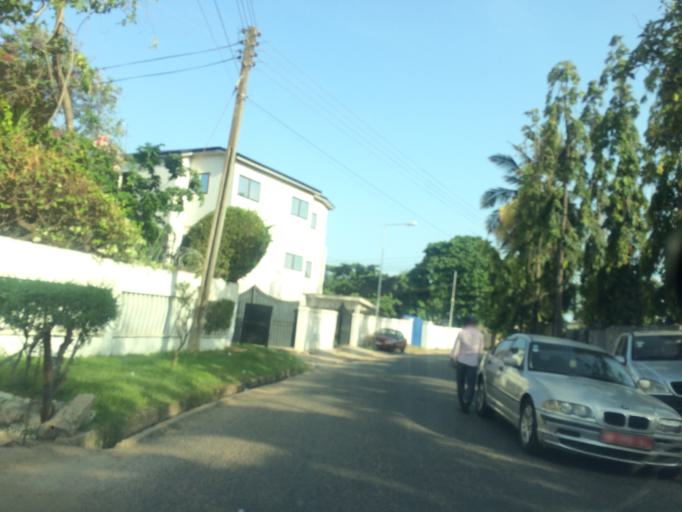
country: GH
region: Greater Accra
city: Accra
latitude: 5.5649
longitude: -0.1791
